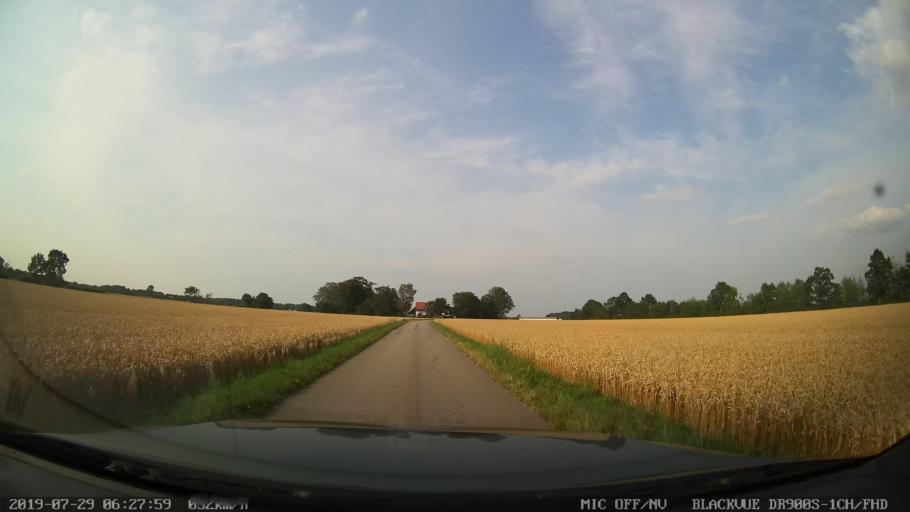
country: SE
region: Skane
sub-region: Helsingborg
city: Odakra
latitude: 56.1112
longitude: 12.7150
